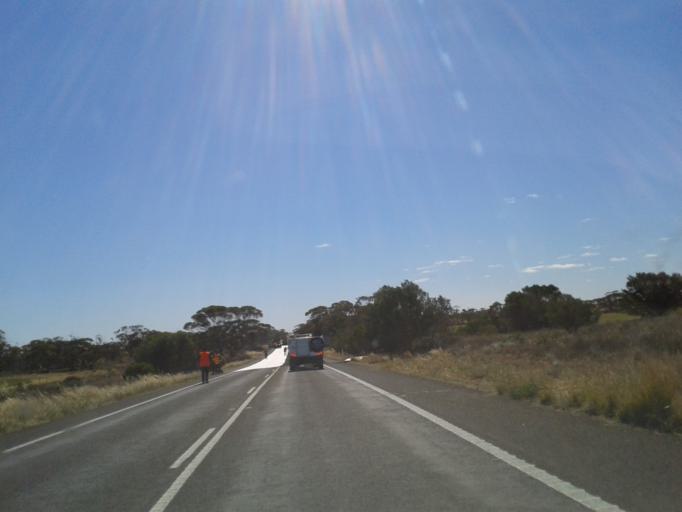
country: AU
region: New South Wales
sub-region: Wentworth
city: Dareton
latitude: -34.2743
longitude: 141.7932
